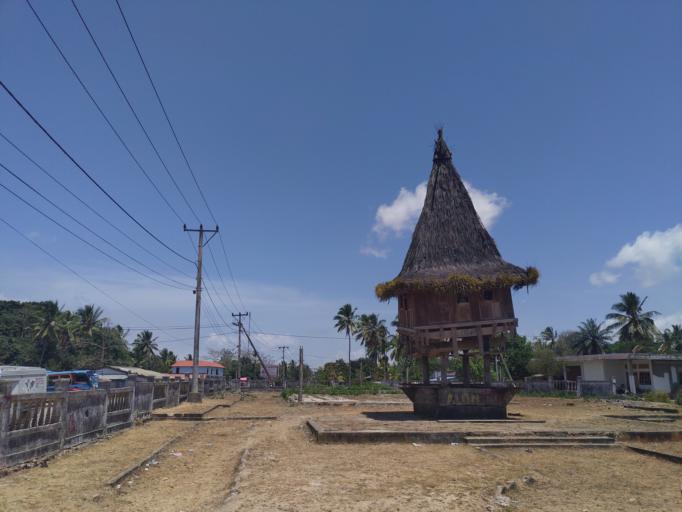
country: TL
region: Lautem
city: Lospalos
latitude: -8.5219
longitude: 126.9986
